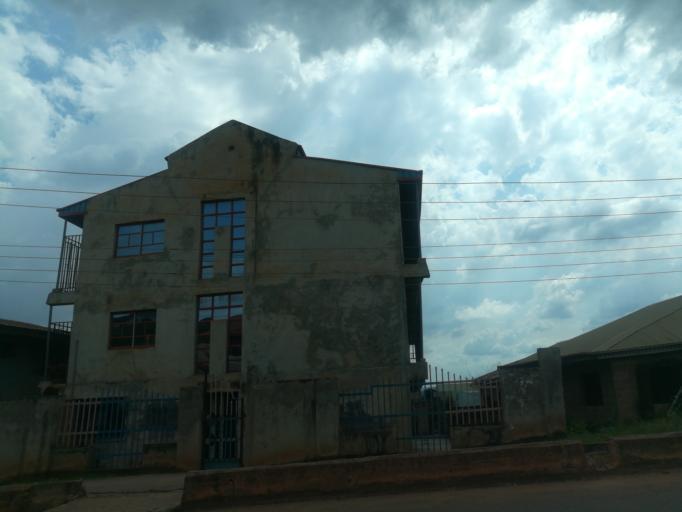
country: NG
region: Oyo
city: Ido
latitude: 7.4354
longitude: 3.8320
